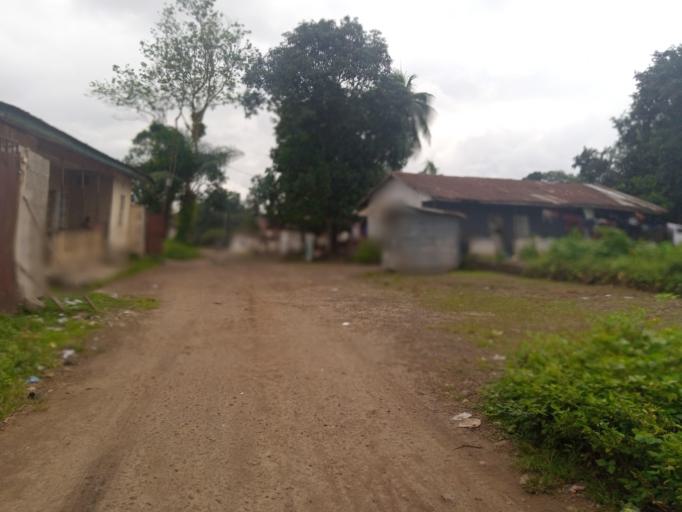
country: SL
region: Eastern Province
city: Kenema
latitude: 7.8623
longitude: -11.1938
